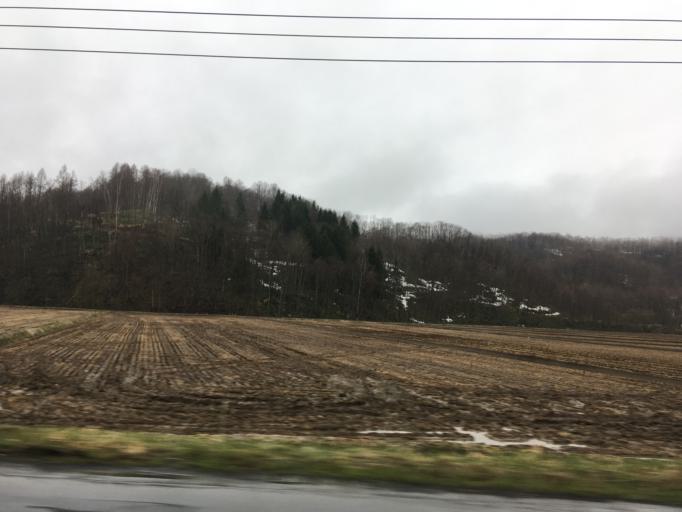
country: JP
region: Hokkaido
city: Nayoro
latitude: 44.0904
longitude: 142.4456
